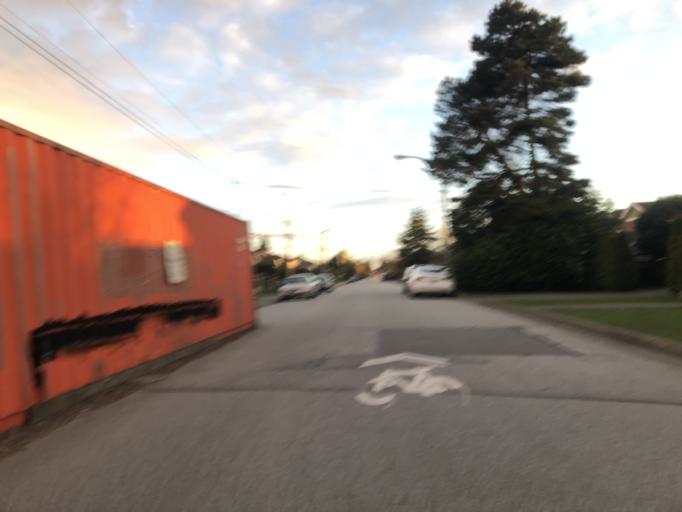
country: CA
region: British Columbia
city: Richmond
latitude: 49.1537
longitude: -123.1197
